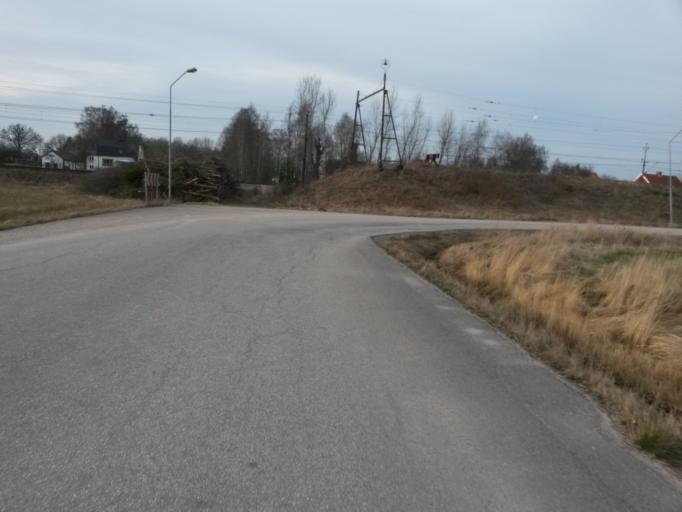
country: SE
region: Vaestra Goetaland
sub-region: Herrljunga Kommun
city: Herrljunga
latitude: 58.0753
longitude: 13.0075
